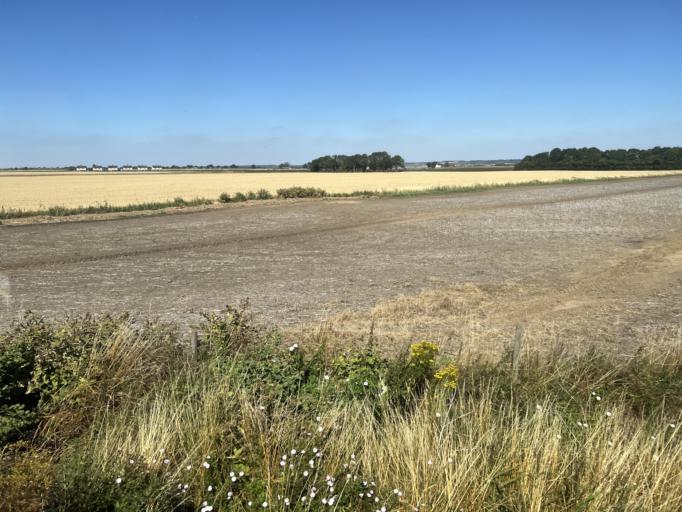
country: GB
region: England
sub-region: Lincolnshire
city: Spilsby
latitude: 53.0967
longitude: 0.1059
